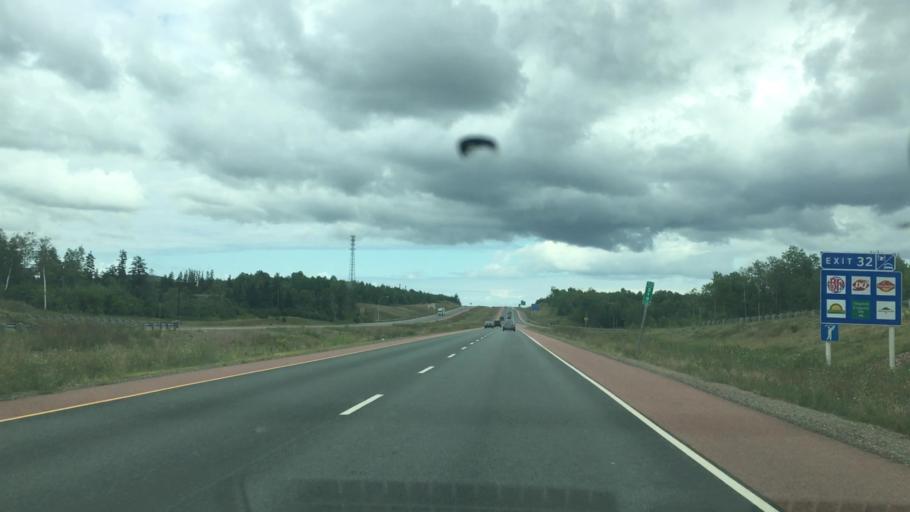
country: CA
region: Nova Scotia
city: Antigonish
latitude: 45.6012
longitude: -62.0229
